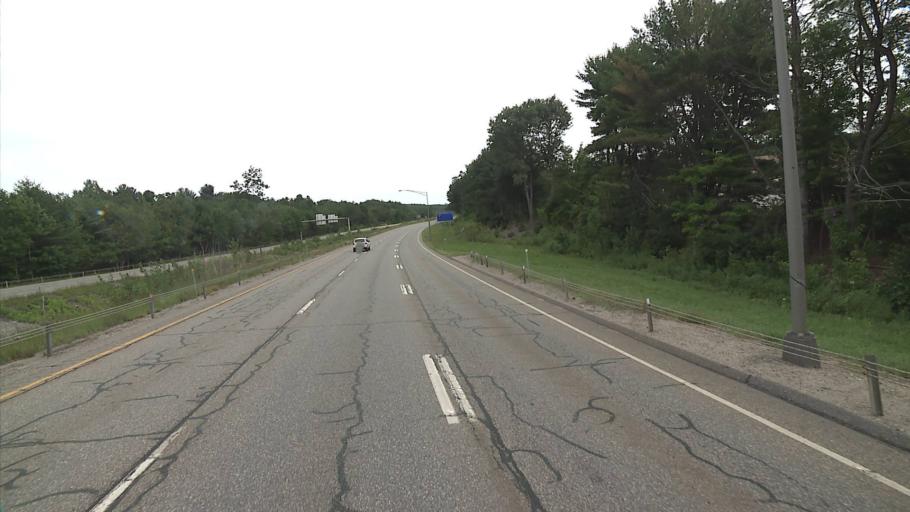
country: US
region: Connecticut
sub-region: Litchfield County
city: Torrington
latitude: 41.8158
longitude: -73.1134
